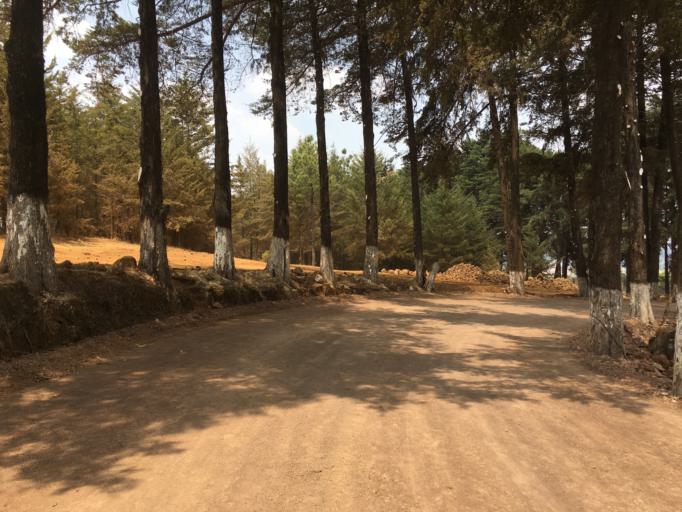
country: MX
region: Michoacan
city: Patzcuaro
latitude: 19.5148
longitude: -101.6306
